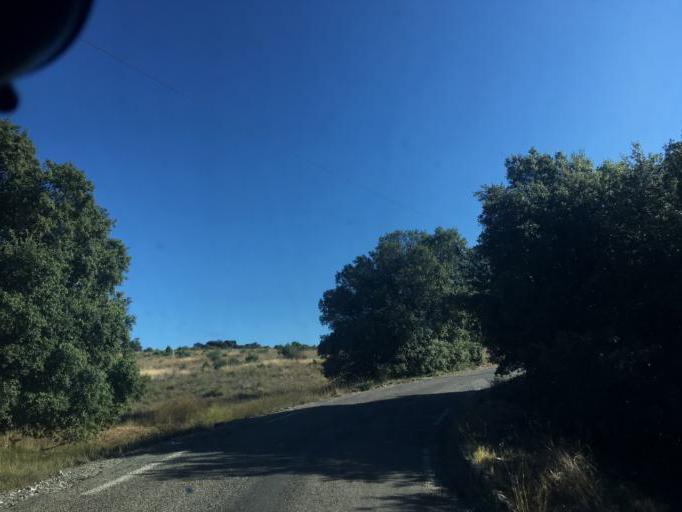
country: FR
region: Provence-Alpes-Cote d'Azur
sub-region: Departement du Var
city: Regusse
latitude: 43.7202
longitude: 6.1313
